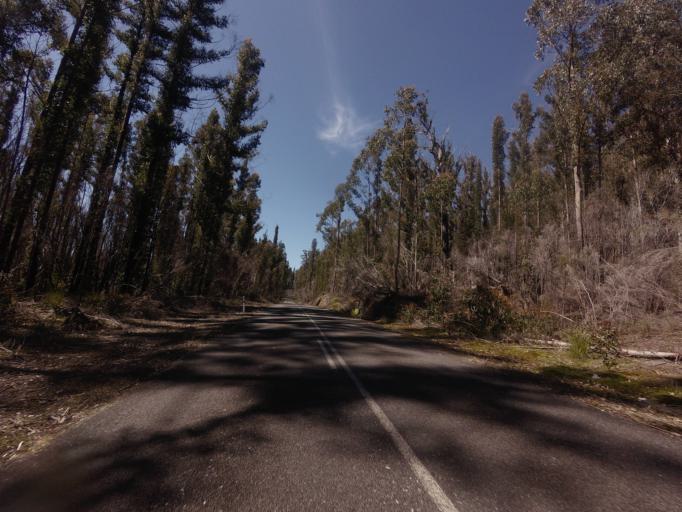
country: AU
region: Tasmania
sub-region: Huon Valley
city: Geeveston
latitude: -42.8435
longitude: 146.2514
